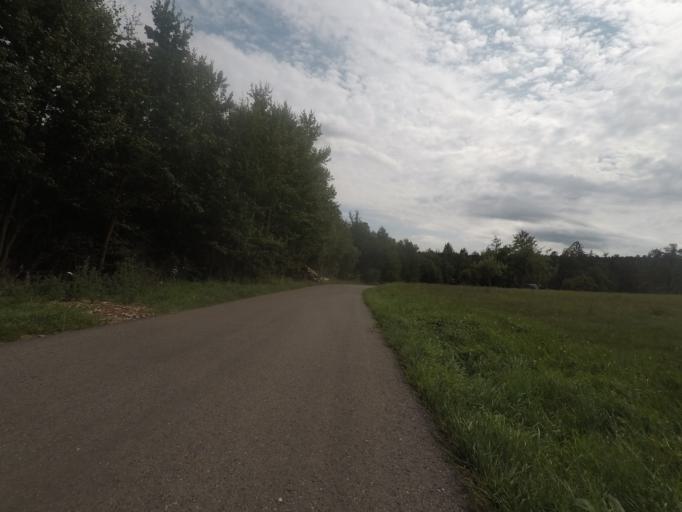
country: DE
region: Baden-Wuerttemberg
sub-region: Karlsruhe Region
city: Bad Herrenalb
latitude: 48.8363
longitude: 8.4564
